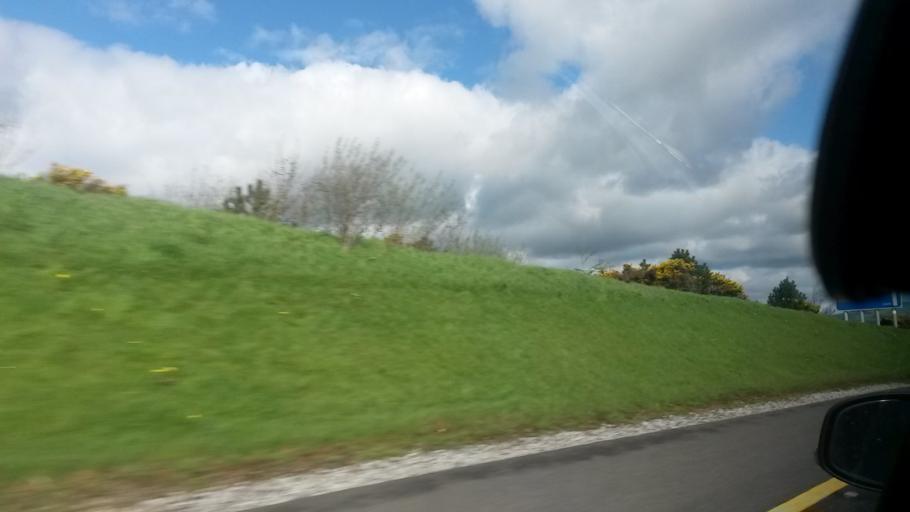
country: IE
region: Munster
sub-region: County Cork
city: Mitchelstown
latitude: 52.2243
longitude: -8.2878
